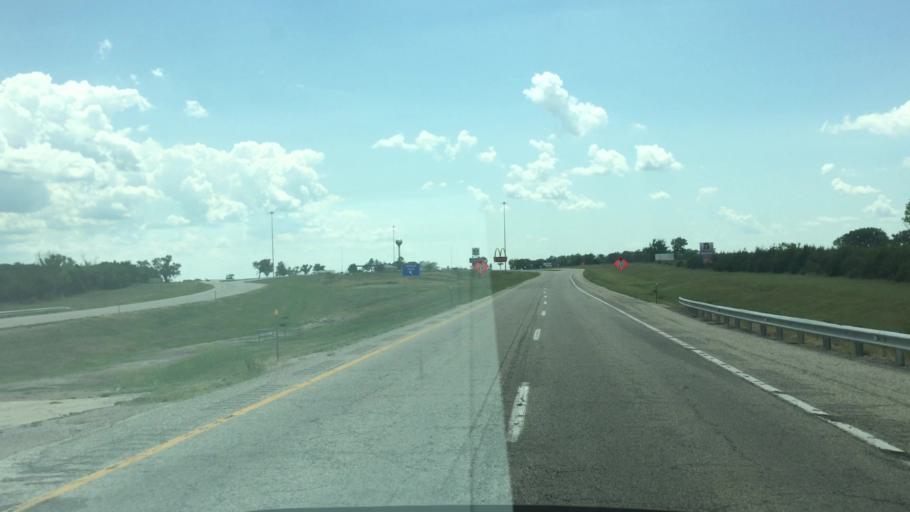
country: US
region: Kansas
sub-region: Lyon County
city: Emporia
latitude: 38.4765
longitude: -96.1805
